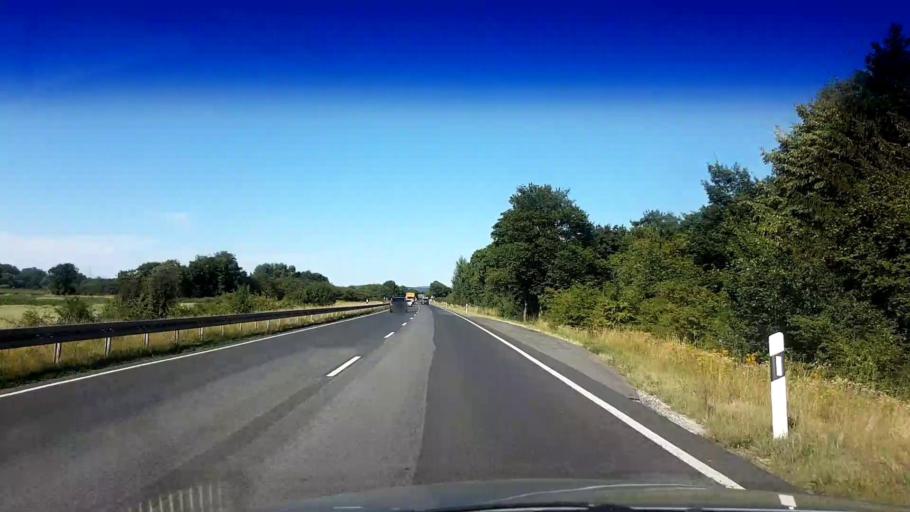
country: DE
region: Bavaria
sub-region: Upper Franconia
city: Bischberg
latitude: 49.9118
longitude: 10.8493
